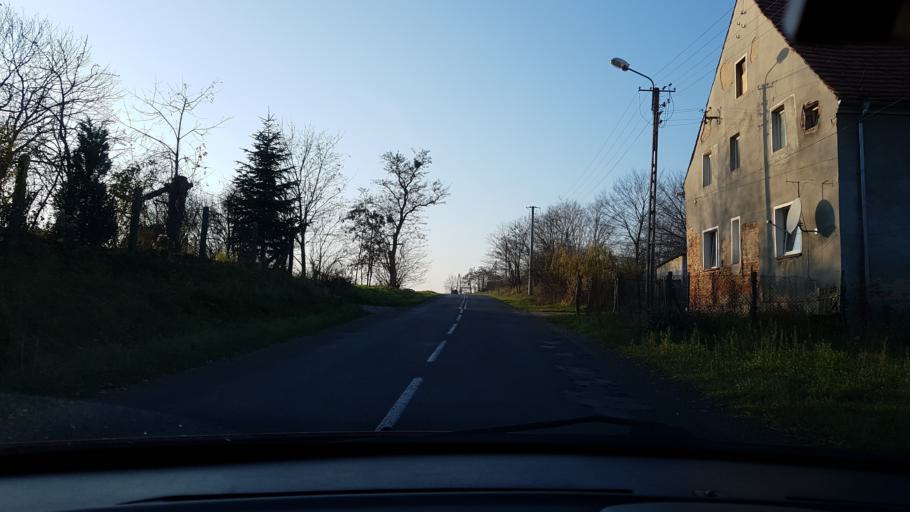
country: PL
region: Lower Silesian Voivodeship
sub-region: Powiat strzelinski
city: Przeworno
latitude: 50.6655
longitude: 17.2703
